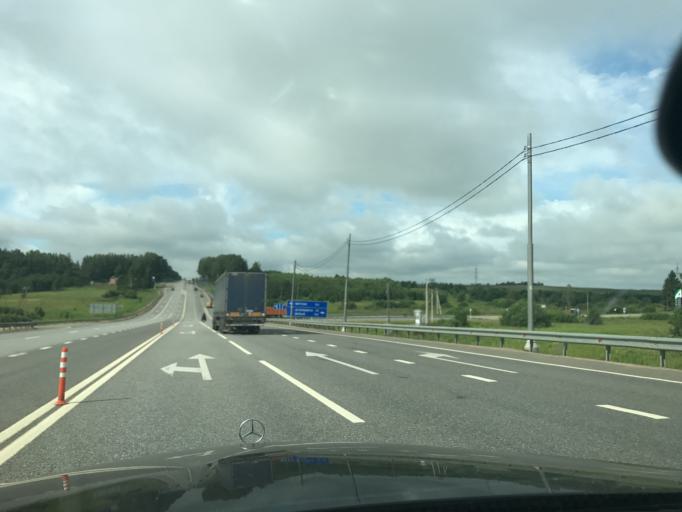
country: RU
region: Smolensk
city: Kardymovo
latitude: 55.0152
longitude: 32.2974
